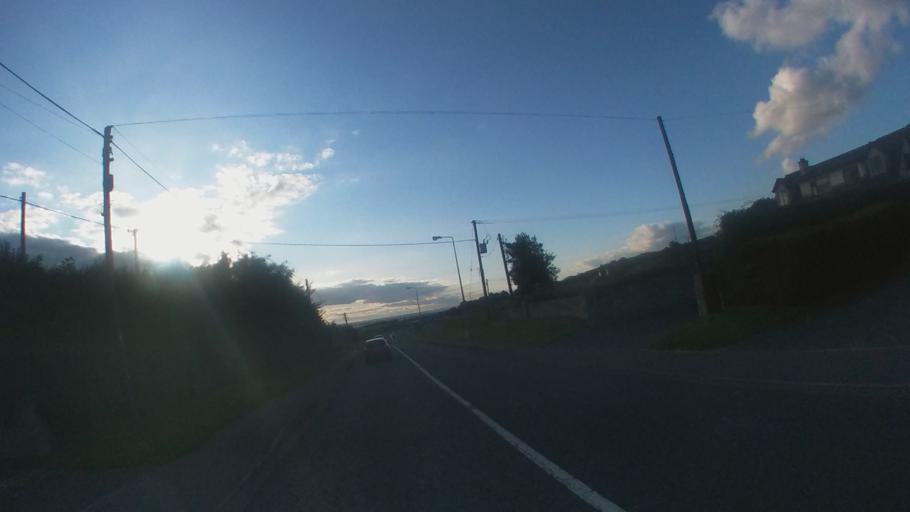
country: IE
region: Leinster
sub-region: Lu
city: Carlingford
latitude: 54.0015
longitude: -6.2742
